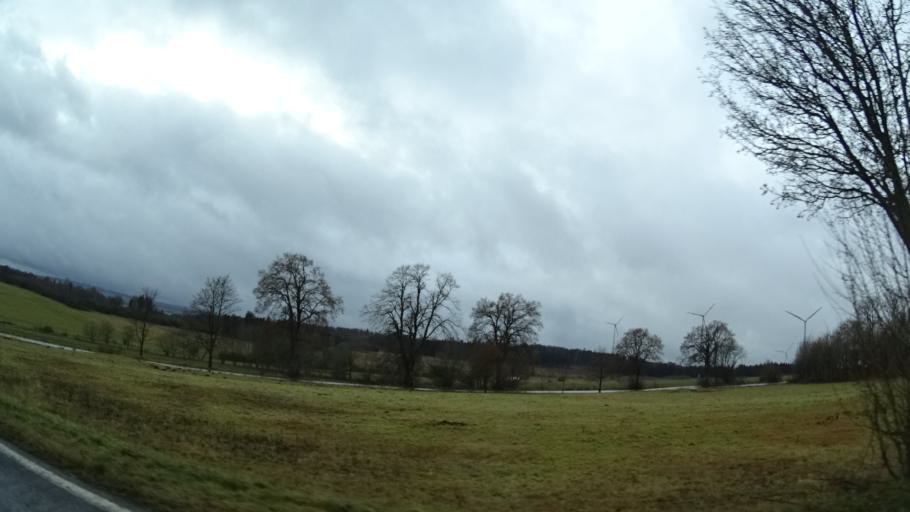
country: DE
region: Hesse
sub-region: Regierungsbezirk Giessen
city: Lautertal
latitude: 50.6068
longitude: 9.2850
